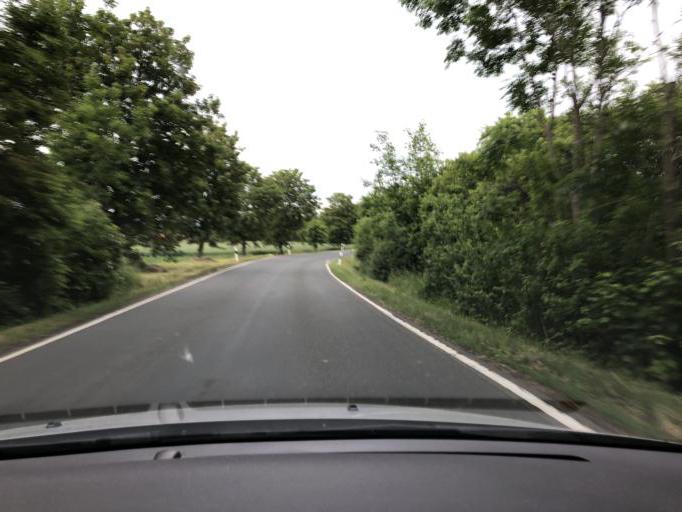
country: DE
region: Thuringia
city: Kleinobringen
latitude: 51.0304
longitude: 11.3056
